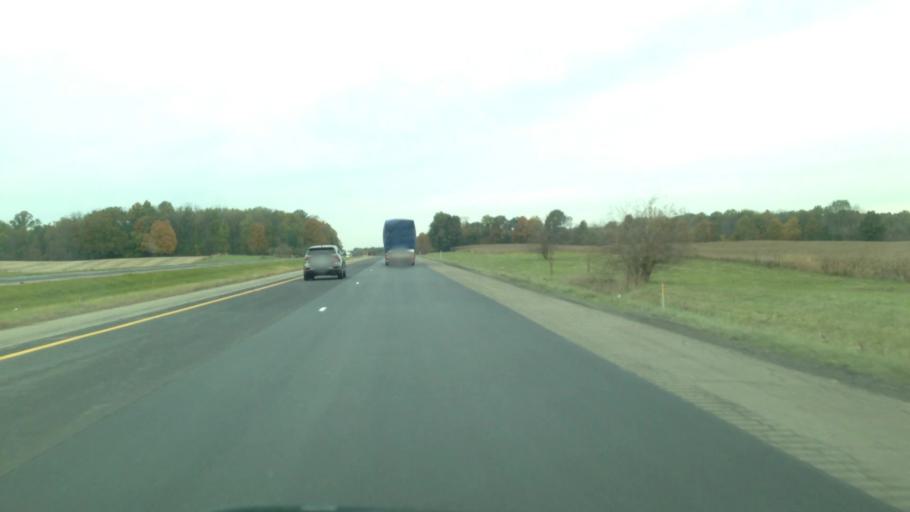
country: US
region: Indiana
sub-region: Steuben County
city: Hamilton
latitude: 41.6330
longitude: -84.8209
